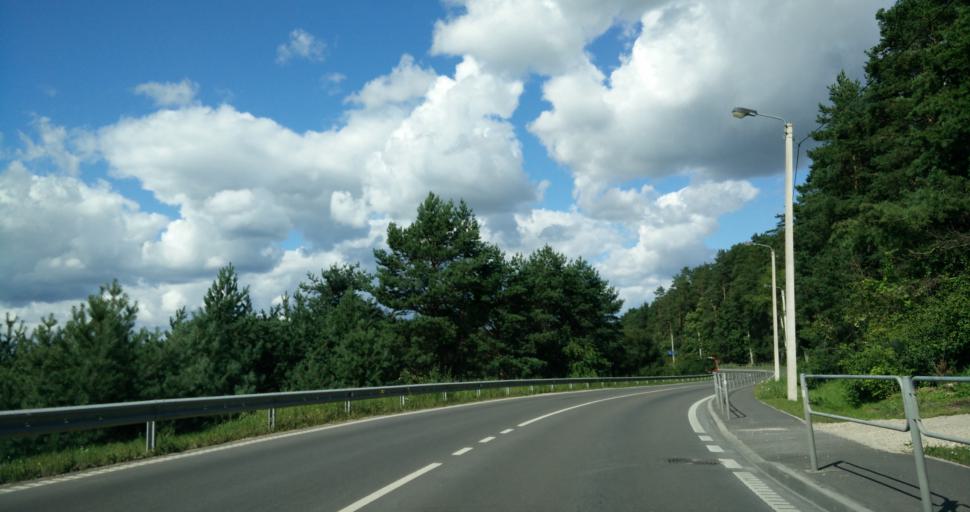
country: LT
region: Kauno apskritis
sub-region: Kauno rajonas
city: Akademija (Kaunas)
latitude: 54.9248
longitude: 23.7932
